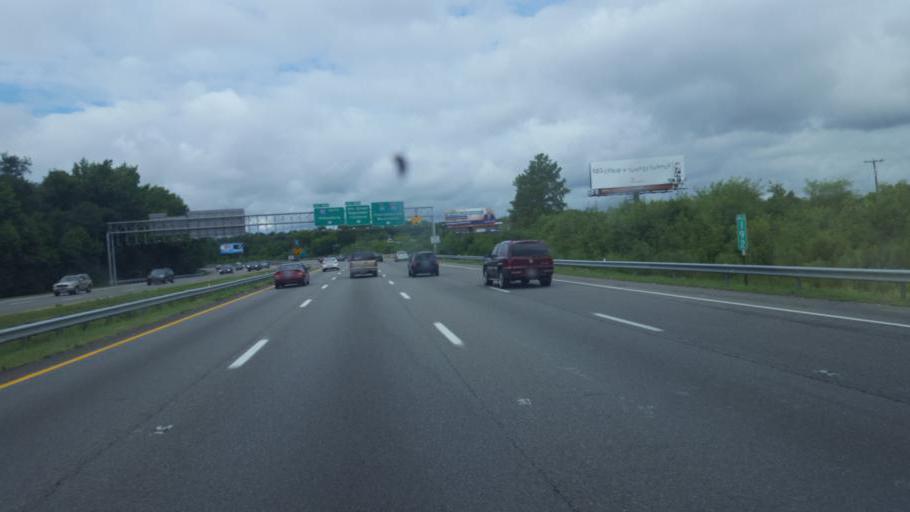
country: US
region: Virginia
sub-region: Henrico County
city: East Highland Park
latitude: 37.5580
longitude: -77.4136
